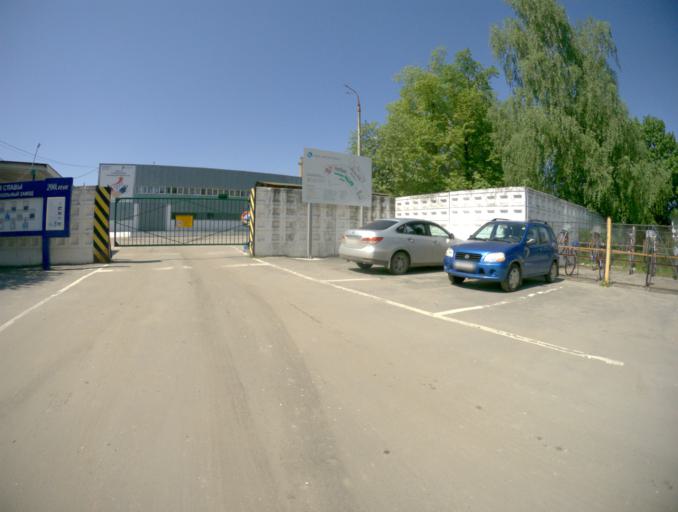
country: RU
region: Vladimir
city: Anopino
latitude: 55.7014
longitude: 40.6619
